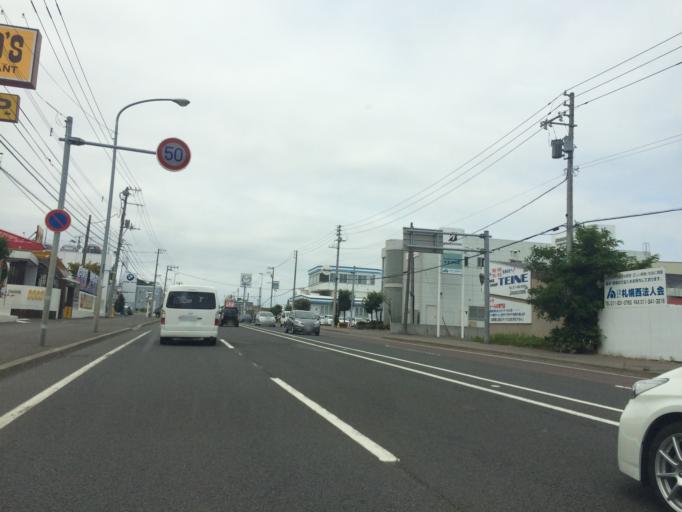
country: JP
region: Hokkaido
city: Sapporo
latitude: 43.1018
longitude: 141.2527
